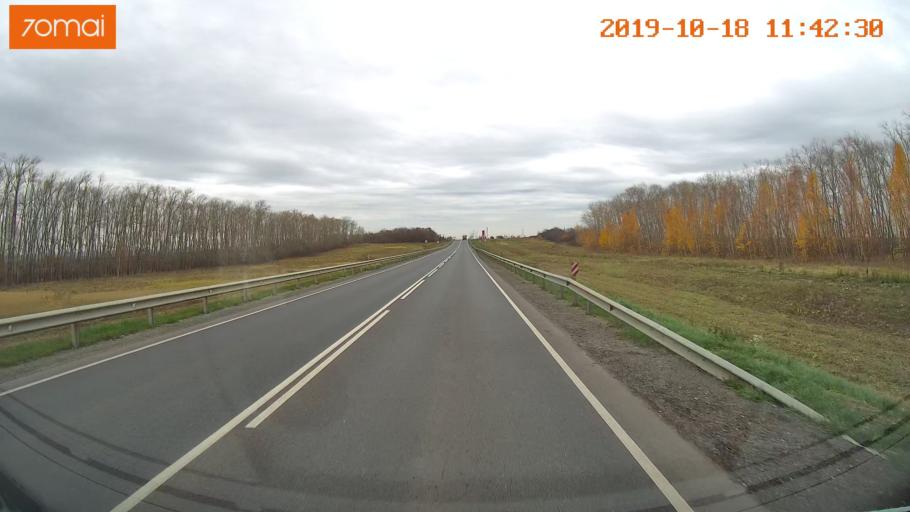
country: RU
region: Rjazan
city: Oktyabr'skiy
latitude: 54.1889
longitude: 38.9290
